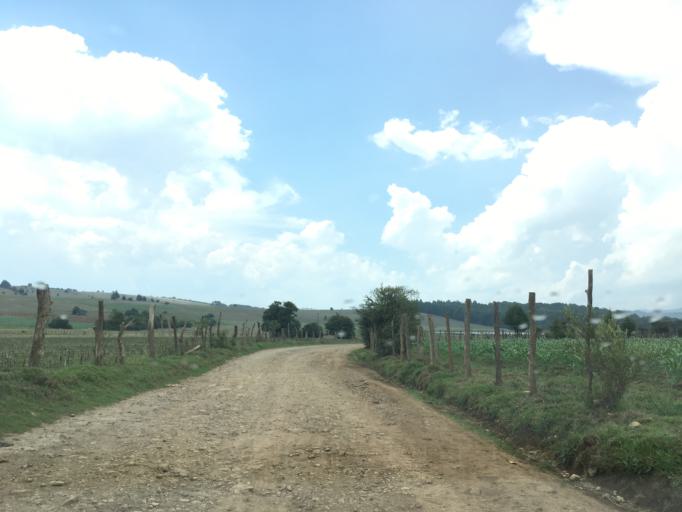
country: MX
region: Michoacan
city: Acuitzio del Canje
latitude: 19.4928
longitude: -101.2350
